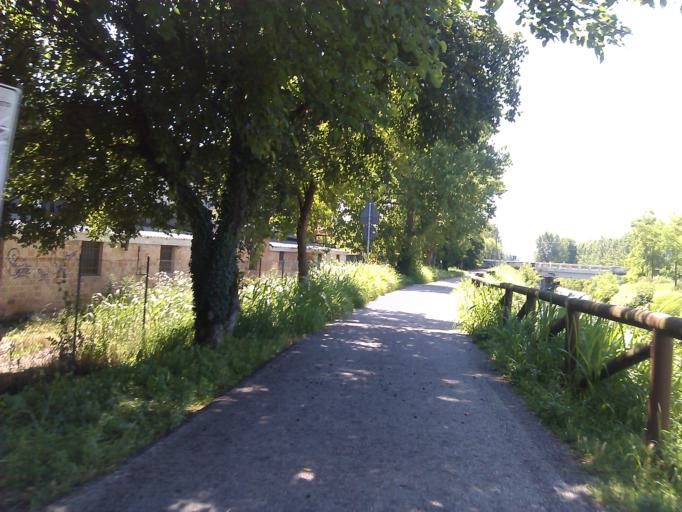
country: IT
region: Veneto
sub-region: Provincia di Treviso
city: Castelfranco Veneto
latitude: 45.6666
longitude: 11.9221
